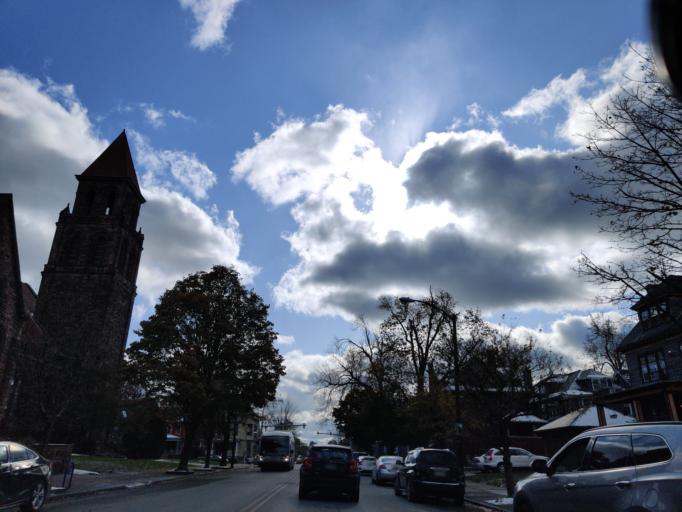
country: US
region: New York
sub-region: Erie County
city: Buffalo
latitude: 42.9212
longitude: -78.8770
